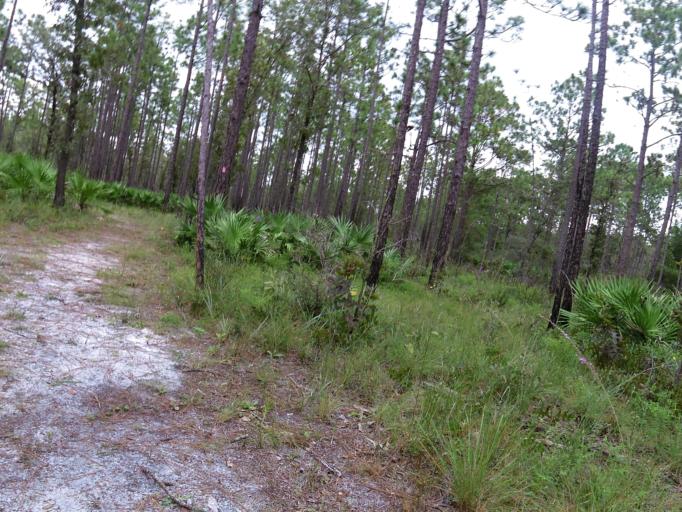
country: US
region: Florida
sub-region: Clay County
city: Middleburg
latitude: 30.1295
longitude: -81.9629
